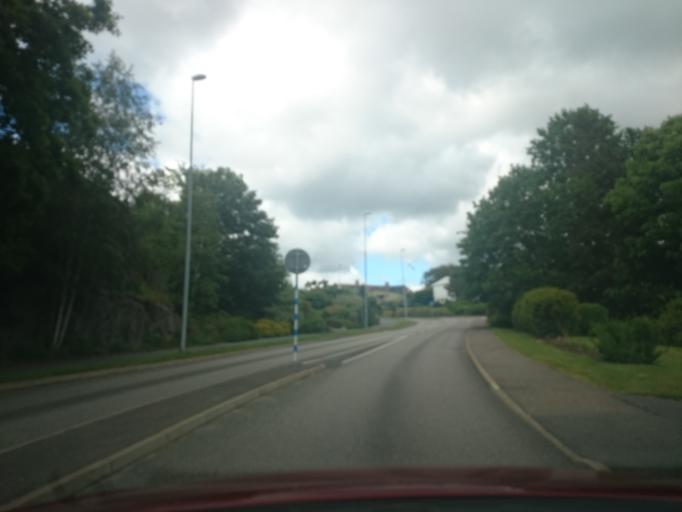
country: SE
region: Vaestra Goetaland
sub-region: Molndal
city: Moelndal
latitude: 57.6593
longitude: 12.0351
